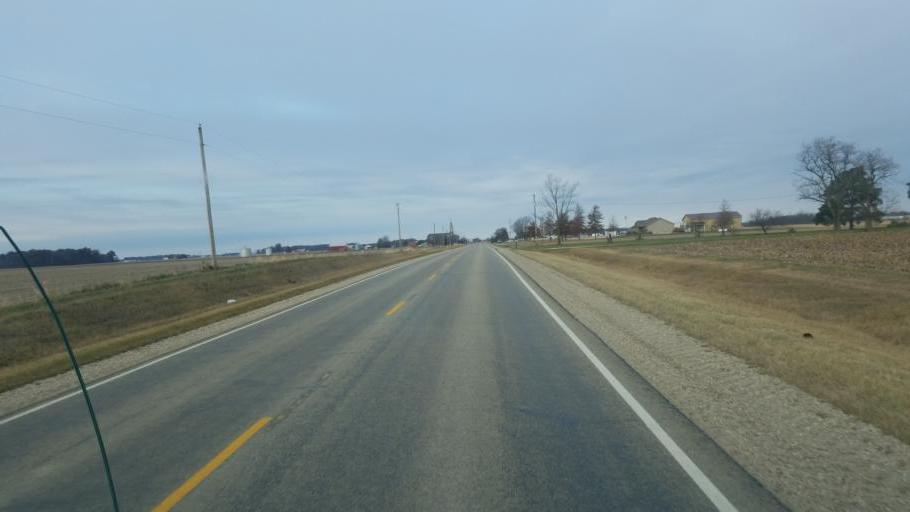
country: US
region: Indiana
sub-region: Adams County
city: Geneva
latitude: 40.5425
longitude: -84.8305
